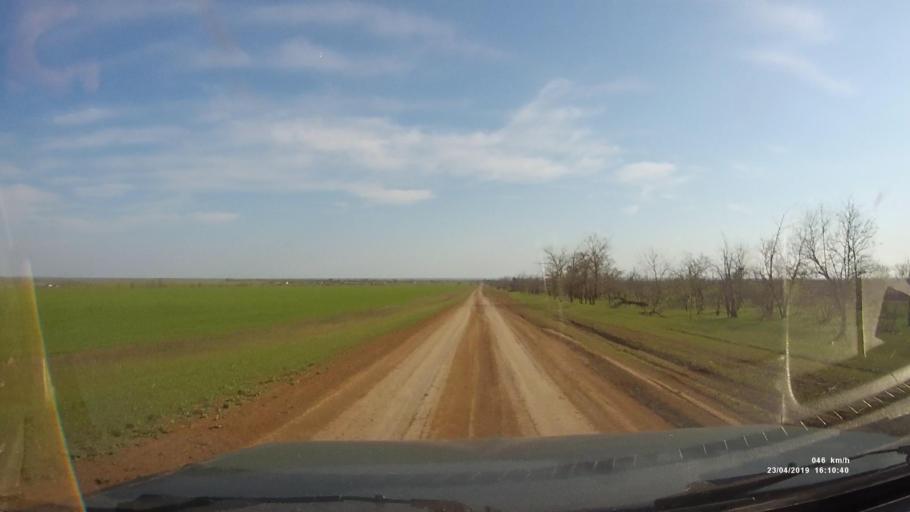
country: RU
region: Rostov
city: Remontnoye
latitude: 46.4804
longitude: 43.1231
